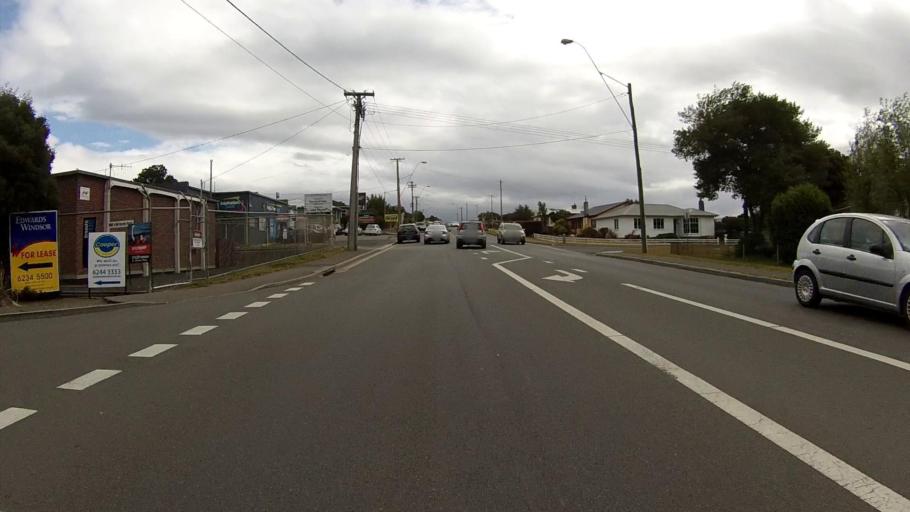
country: AU
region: Tasmania
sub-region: Clarence
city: Warrane
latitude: -42.8571
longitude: 147.3923
